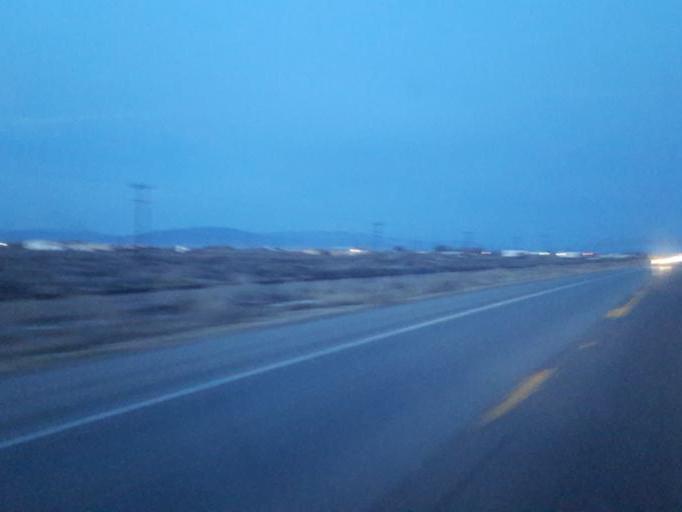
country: US
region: Colorado
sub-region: Alamosa County
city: Alamosa
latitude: 37.4871
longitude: -105.9228
